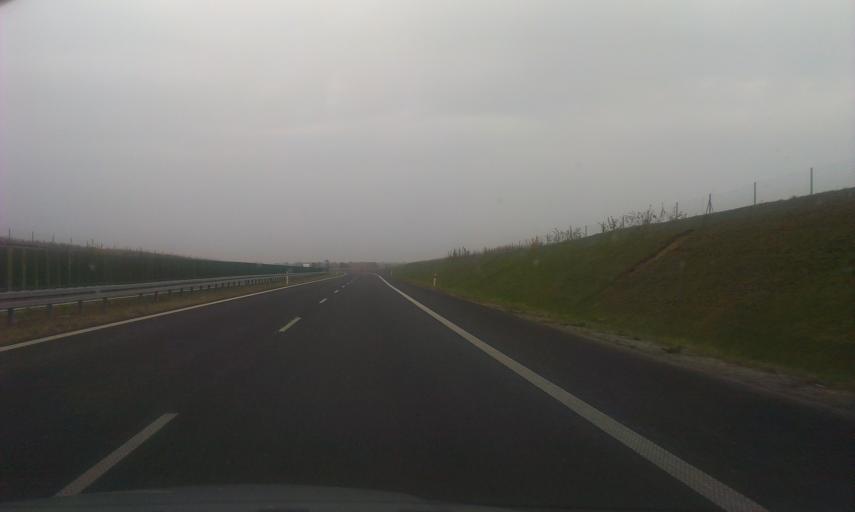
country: PL
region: Greater Poland Voivodeship
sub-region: Powiat poznanski
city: Zlotniki
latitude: 52.5151
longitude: 16.8063
